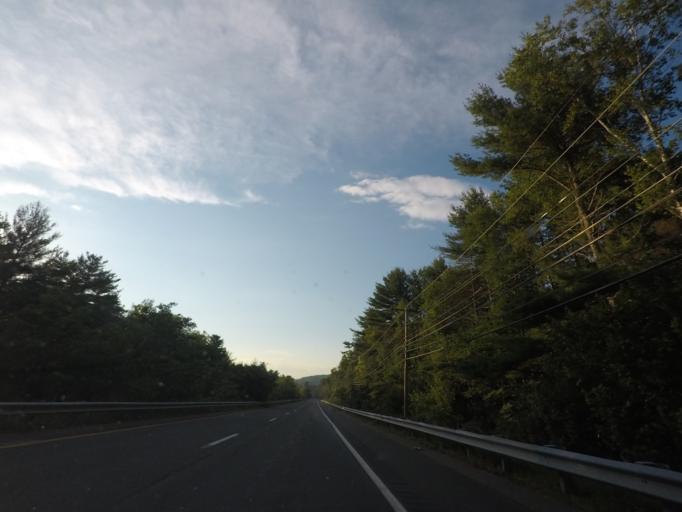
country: US
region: Massachusetts
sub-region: Hampden County
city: Brimfield
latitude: 42.1244
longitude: -72.2514
